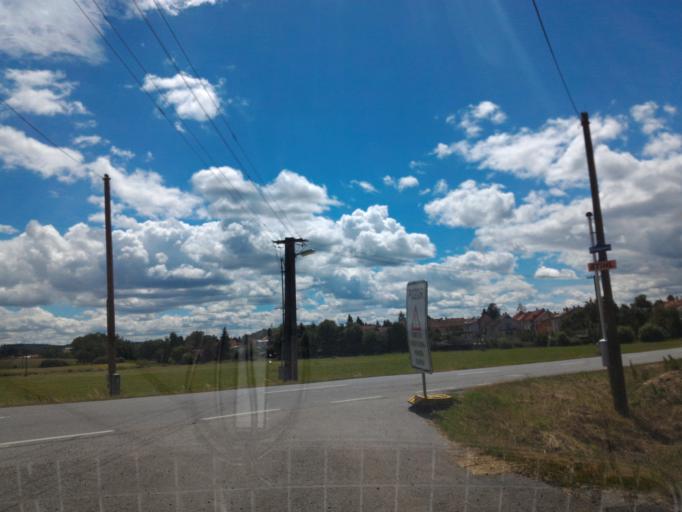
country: CZ
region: Vysocina
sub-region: Okres Jihlava
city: Telc
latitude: 49.1927
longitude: 15.4507
